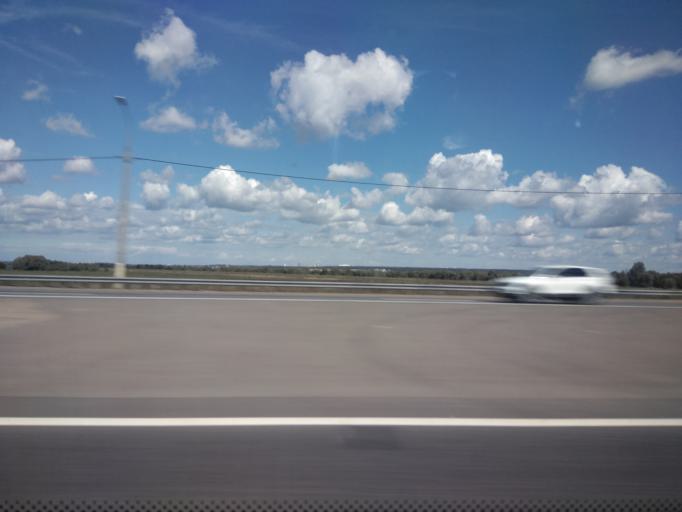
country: RU
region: Moskovskaya
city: Danki
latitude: 54.8640
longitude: 37.4988
